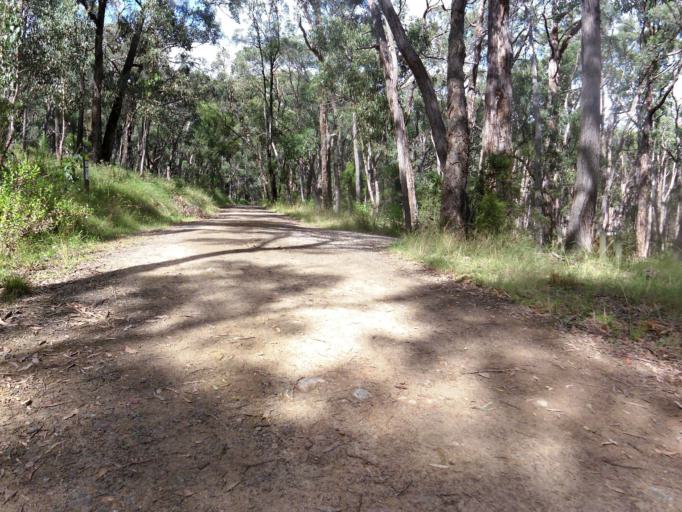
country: AU
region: Victoria
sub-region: Knox
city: The Basin
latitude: -37.8394
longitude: 145.3341
